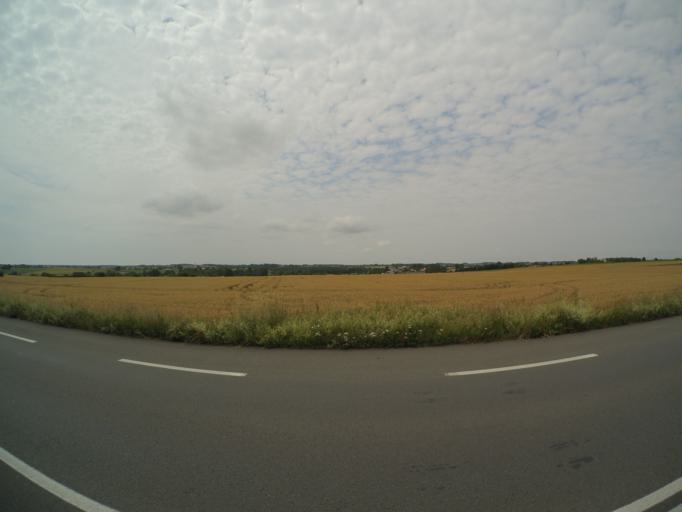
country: FR
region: Pays de la Loire
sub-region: Departement de la Vendee
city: Chavagnes-en-Paillers
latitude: 46.9094
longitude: -1.2377
